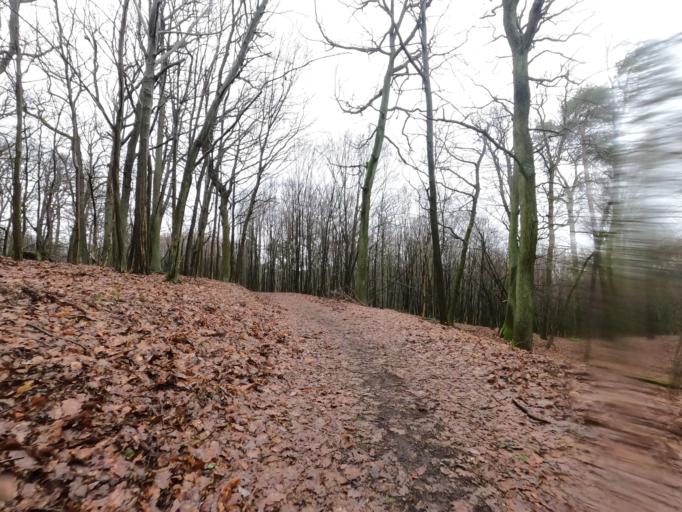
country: PL
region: Greater Poland Voivodeship
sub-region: Powiat pilski
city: Wyrzysk
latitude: 53.1268
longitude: 17.2558
